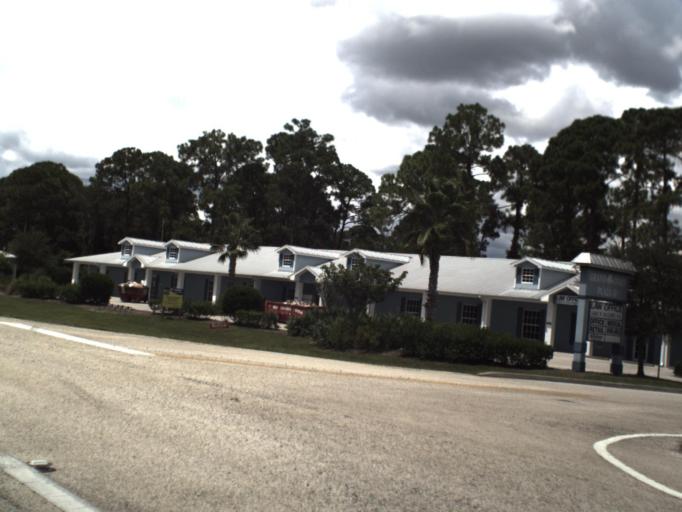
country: US
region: Florida
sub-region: Charlotte County
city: Port Charlotte
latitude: 27.0182
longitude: -82.1579
